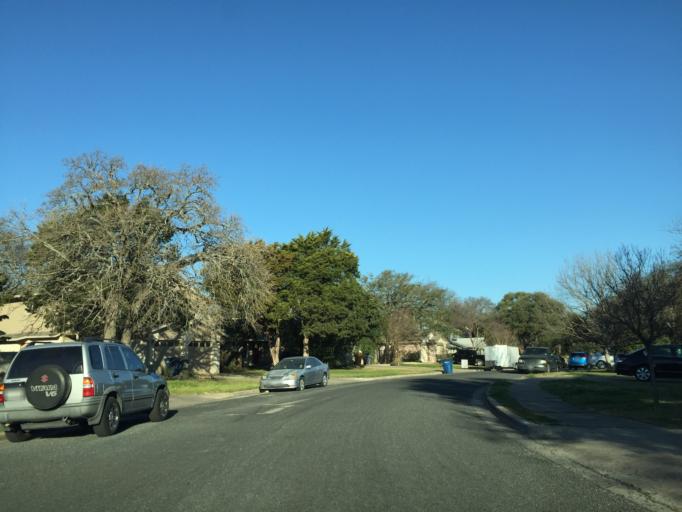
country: US
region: Texas
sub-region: Williamson County
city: Jollyville
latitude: 30.4398
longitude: -97.7685
